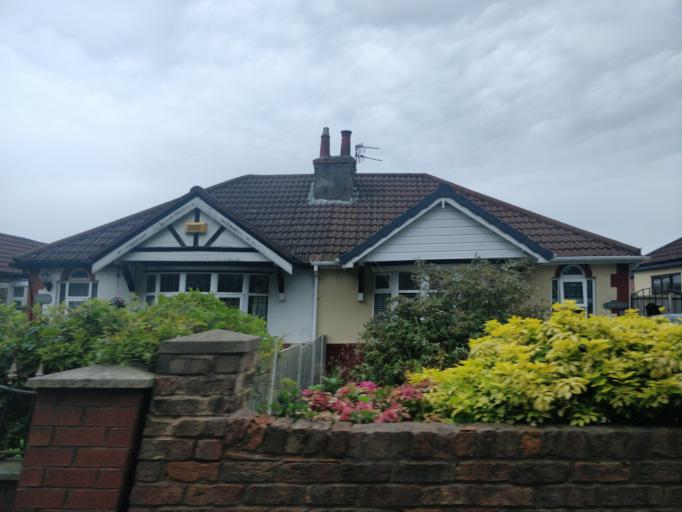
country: GB
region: England
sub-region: Lancashire
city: Ormskirk
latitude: 53.6135
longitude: -2.9282
